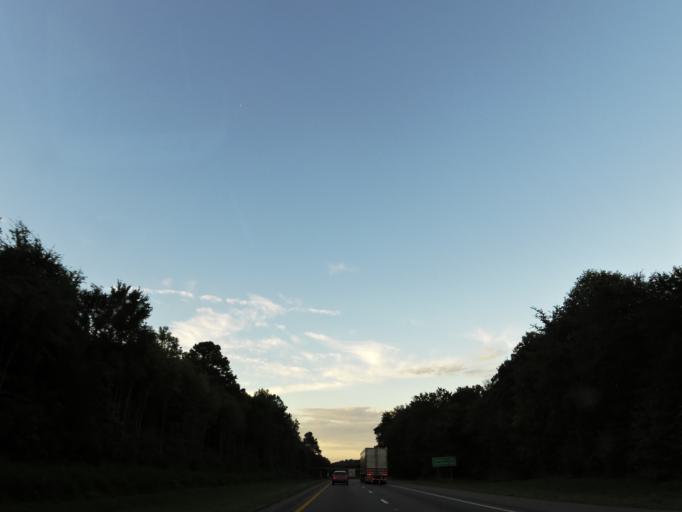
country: US
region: Tennessee
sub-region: McMinn County
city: Athens
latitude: 35.4038
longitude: -84.7073
